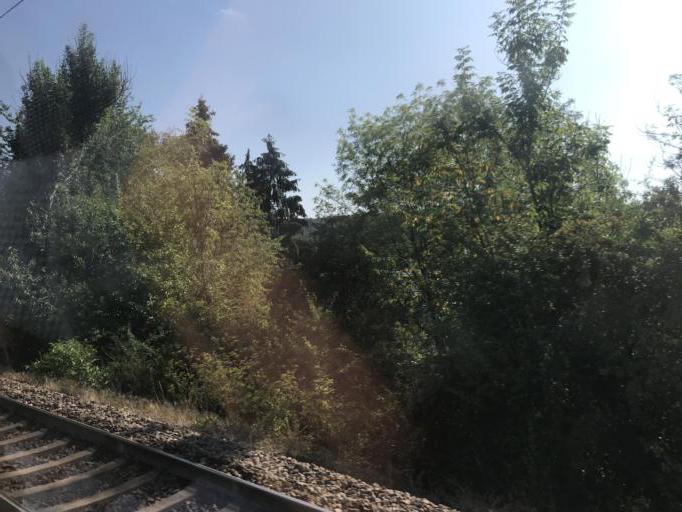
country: DE
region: Saarland
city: Sulzbach
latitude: 49.2831
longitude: 7.0361
